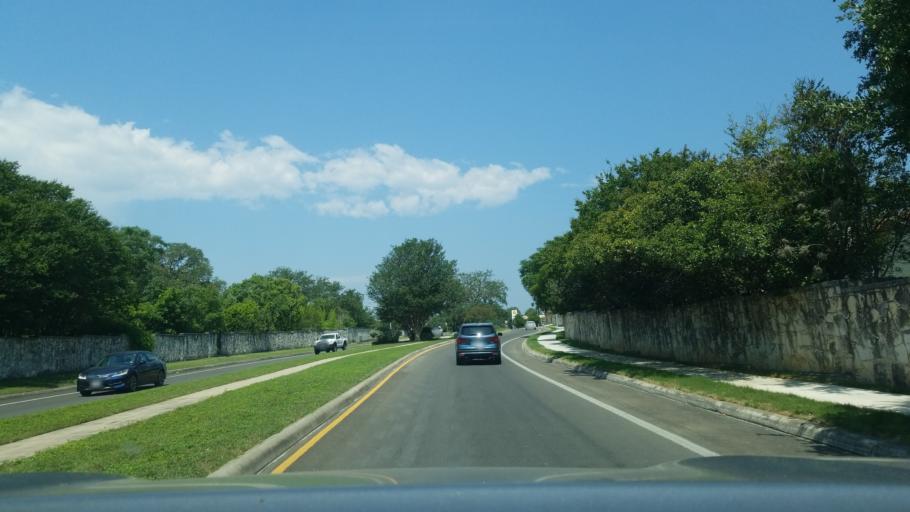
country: US
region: Texas
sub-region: Bexar County
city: Hollywood Park
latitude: 29.6298
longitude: -98.4518
